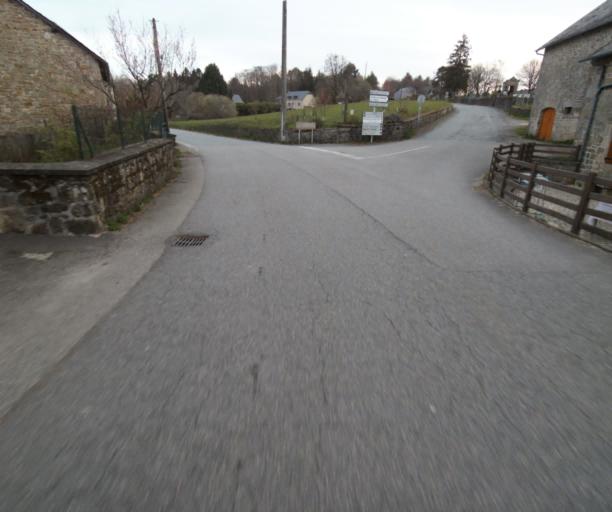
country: FR
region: Limousin
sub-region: Departement de la Correze
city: Correze
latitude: 45.4252
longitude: 1.8361
